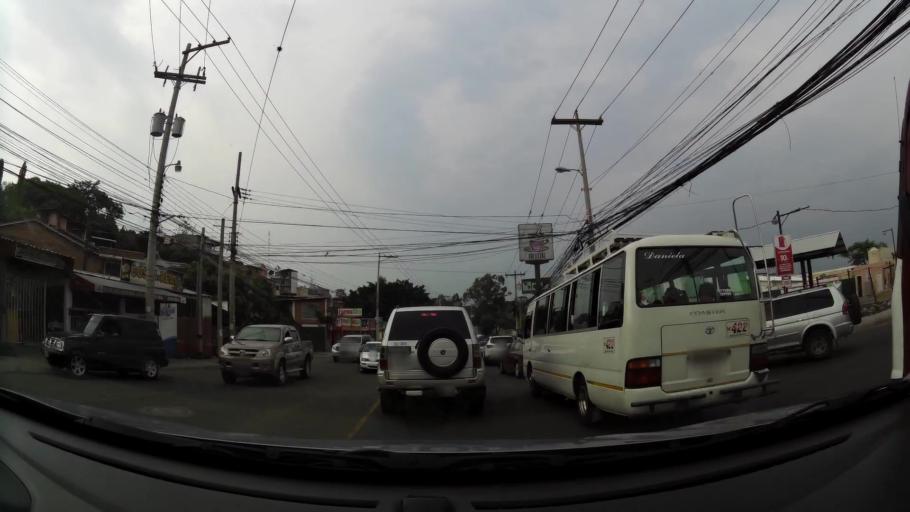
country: HN
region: Francisco Morazan
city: Tegucigalpa
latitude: 14.0621
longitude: -87.2236
